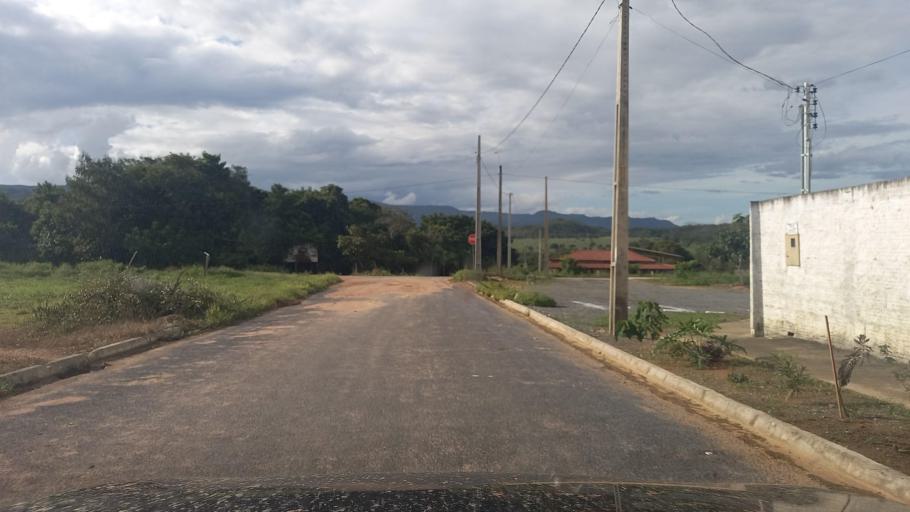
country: BR
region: Goias
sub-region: Cavalcante
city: Cavalcante
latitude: -13.7960
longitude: -47.4465
